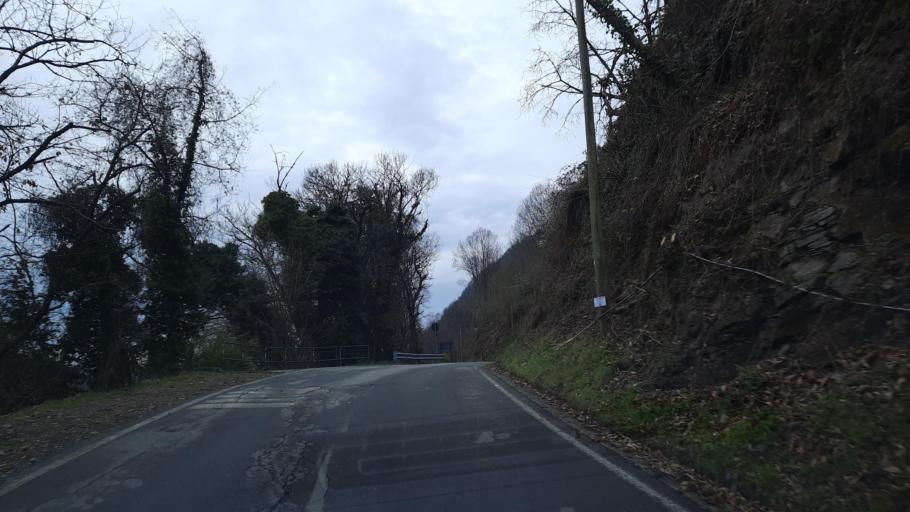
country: IT
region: Piedmont
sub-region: Provincia Verbano-Cusio-Ossola
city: Cesara
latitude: 45.8262
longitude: 8.3811
